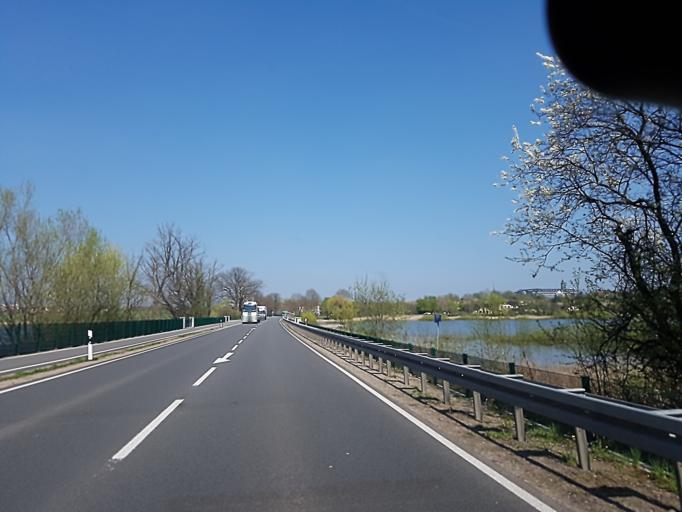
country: DE
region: Saxony
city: Wermsdorf
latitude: 51.2726
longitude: 12.9239
